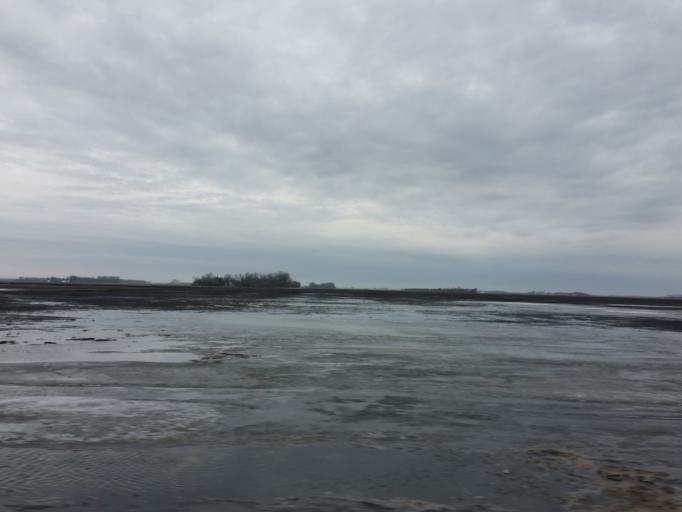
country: US
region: North Dakota
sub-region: Walsh County
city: Grafton
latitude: 48.3914
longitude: -97.4704
